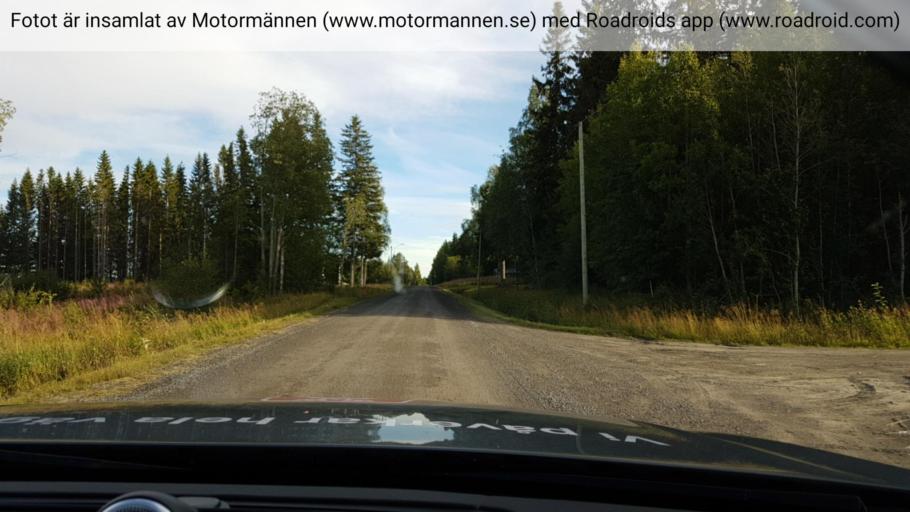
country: SE
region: Jaemtland
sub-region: Stroemsunds Kommun
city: Stroemsund
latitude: 64.1213
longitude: 15.8056
